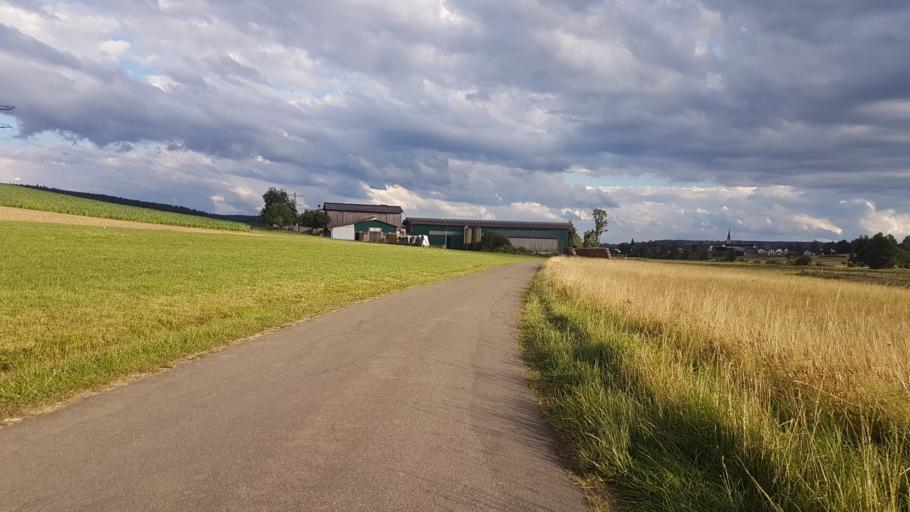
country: DE
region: Baden-Wuerttemberg
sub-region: Freiburg Region
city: Braunlingen
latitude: 47.9801
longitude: 8.4281
